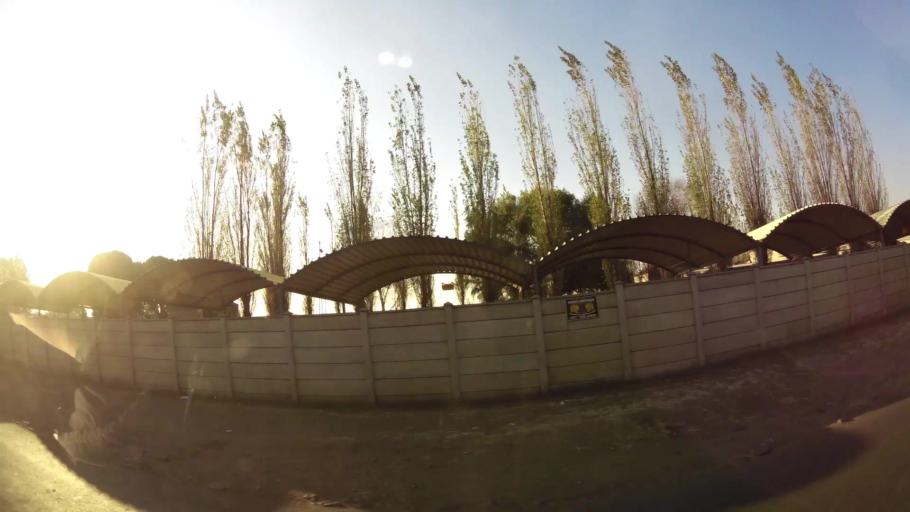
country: ZA
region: Gauteng
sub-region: West Rand District Municipality
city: Randfontein
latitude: -26.1922
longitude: 27.6867
